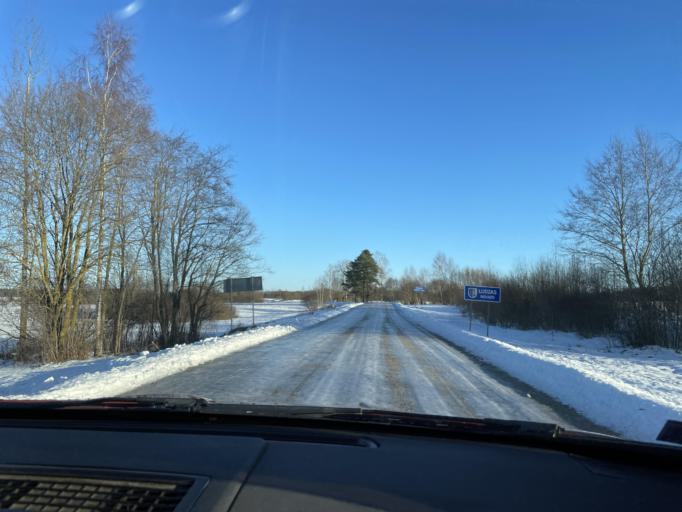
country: LV
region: Ludzas Rajons
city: Ludza
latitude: 56.4553
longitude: 27.5612
